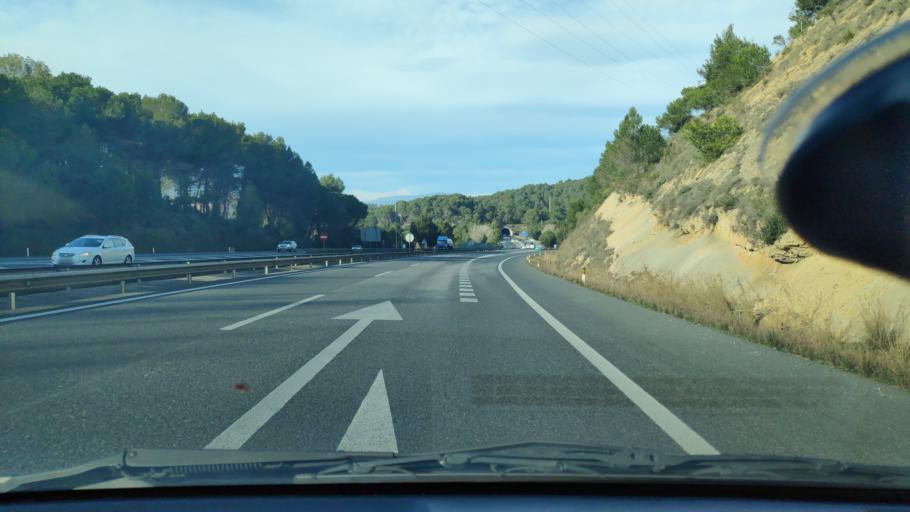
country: ES
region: Catalonia
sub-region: Provincia de Barcelona
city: Rubi
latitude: 41.5064
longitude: 2.0497
